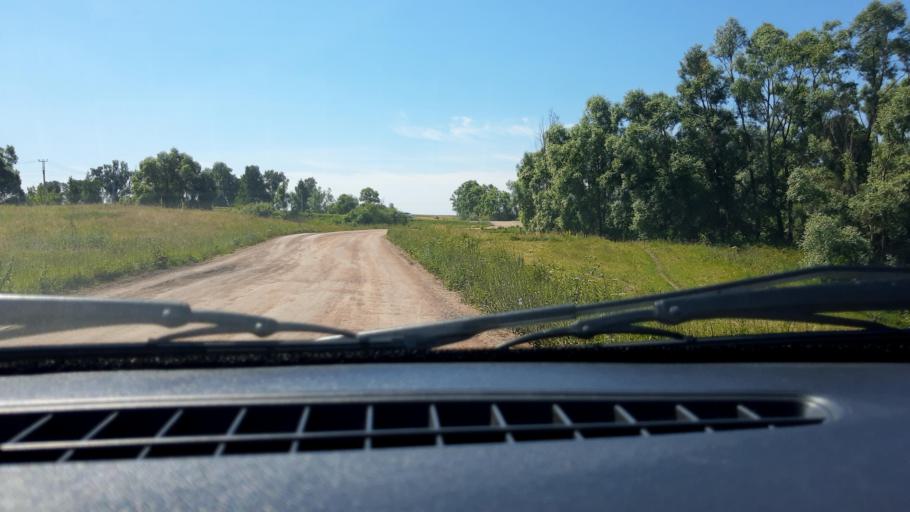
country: RU
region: Bashkortostan
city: Karmaskaly
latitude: 54.3580
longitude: 55.9030
